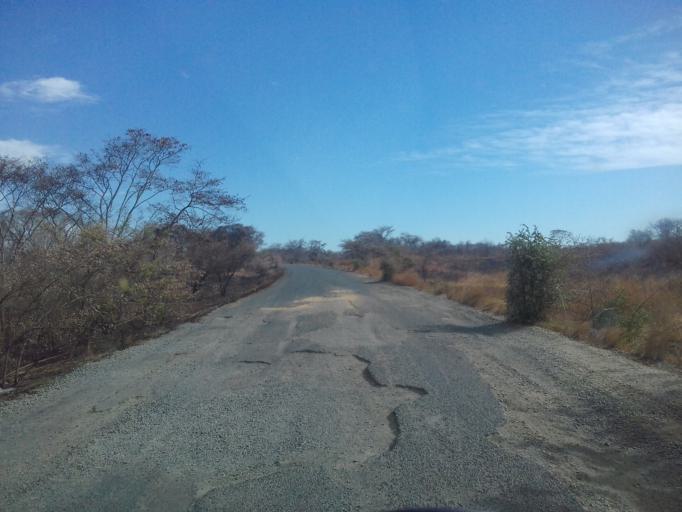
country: MG
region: Sofia
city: Antsohihy
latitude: -15.2249
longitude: 47.8251
